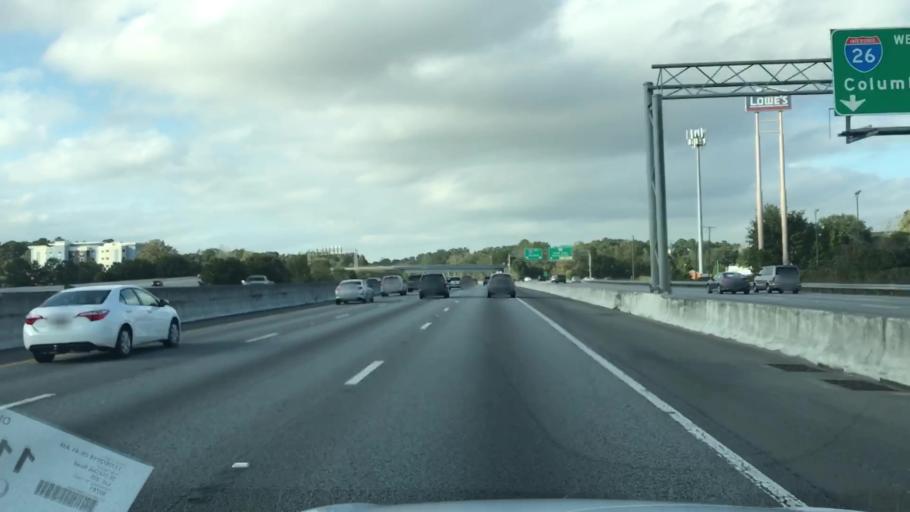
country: US
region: South Carolina
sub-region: Berkeley County
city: Hanahan
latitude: 32.9372
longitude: -80.0487
